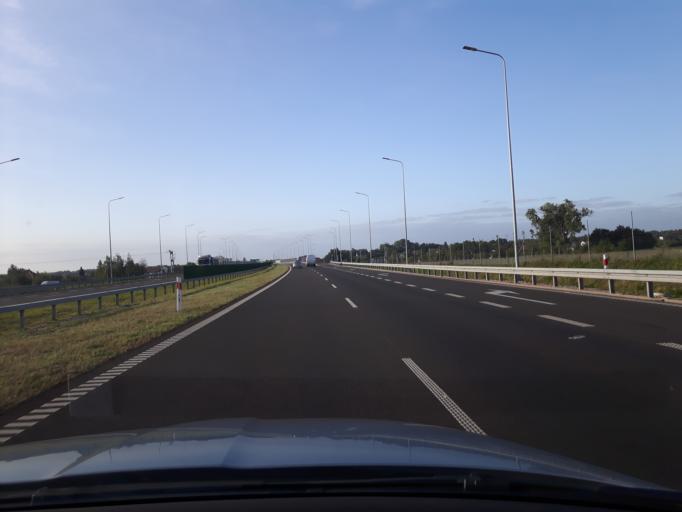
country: PL
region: Masovian Voivodeship
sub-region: Powiat radomski
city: Wolanow
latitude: 51.3926
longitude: 21.0216
